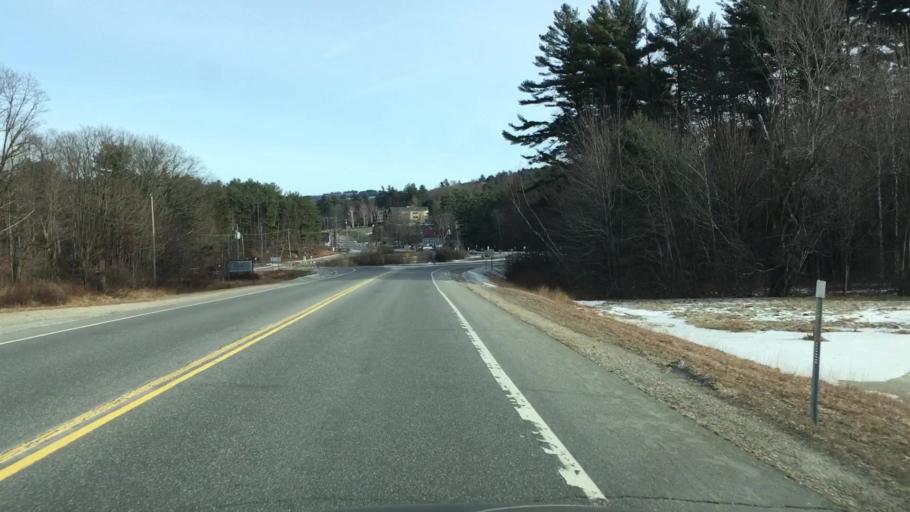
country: US
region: New Hampshire
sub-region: Merrimack County
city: Newbury
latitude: 43.3411
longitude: -72.0743
